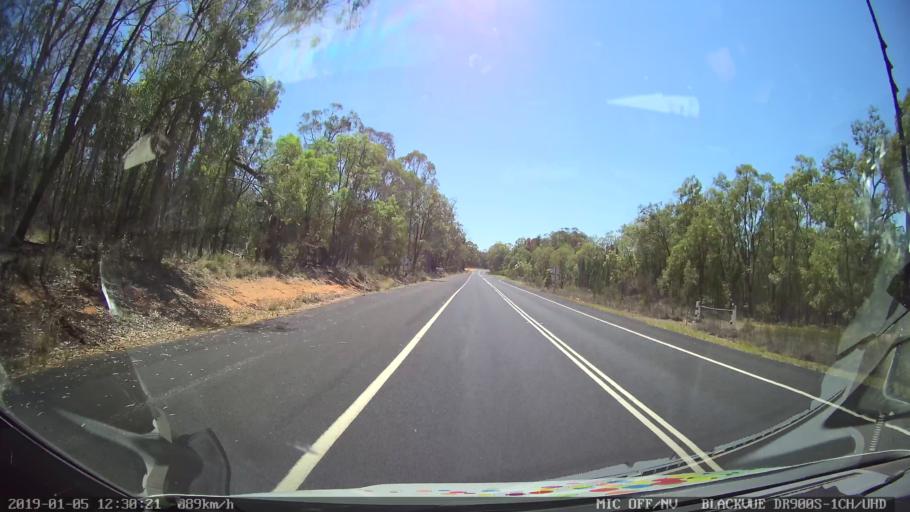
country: AU
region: New South Wales
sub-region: Warrumbungle Shire
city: Coonabarabran
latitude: -31.2285
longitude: 149.3494
